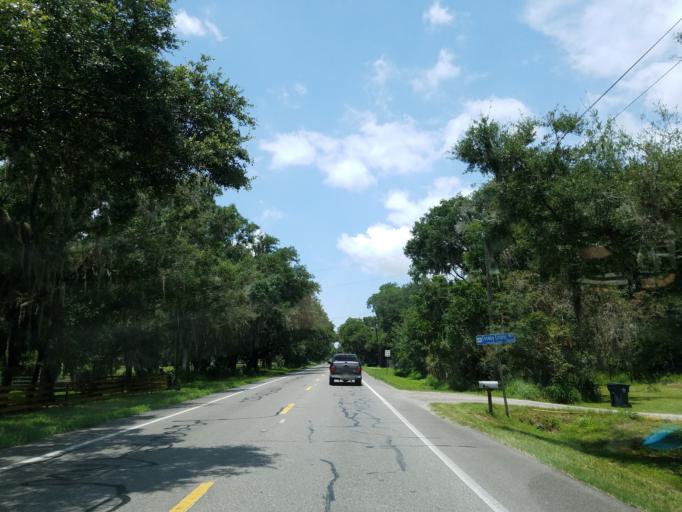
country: US
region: Florida
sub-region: Hillsborough County
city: Fish Hawk
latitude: 27.8506
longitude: -82.1386
